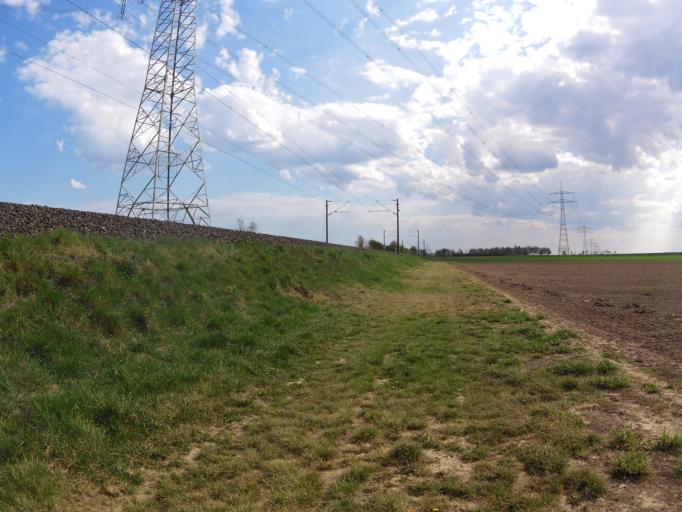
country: DE
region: Bavaria
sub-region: Regierungsbezirk Unterfranken
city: Oberpleichfeld
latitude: 49.8646
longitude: 10.1001
